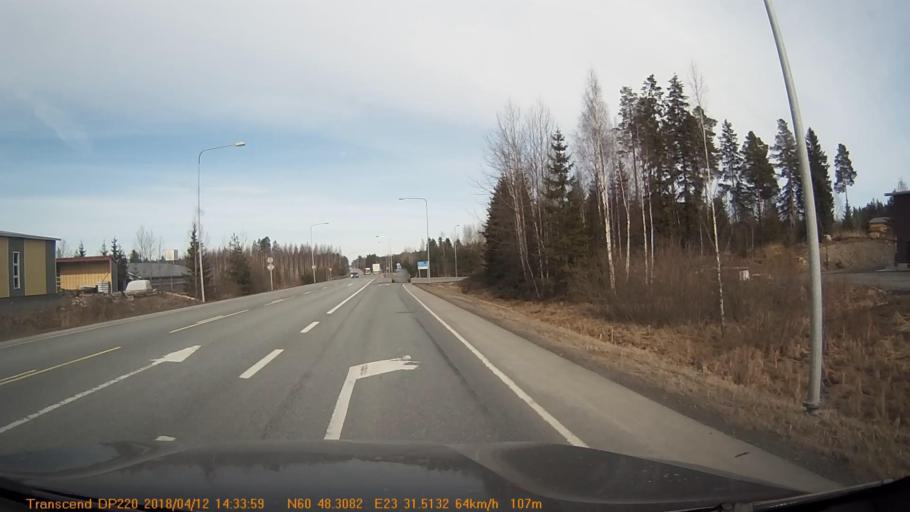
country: FI
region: Haeme
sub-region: Forssa
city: Jokioinen
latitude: 60.8054
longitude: 23.5258
